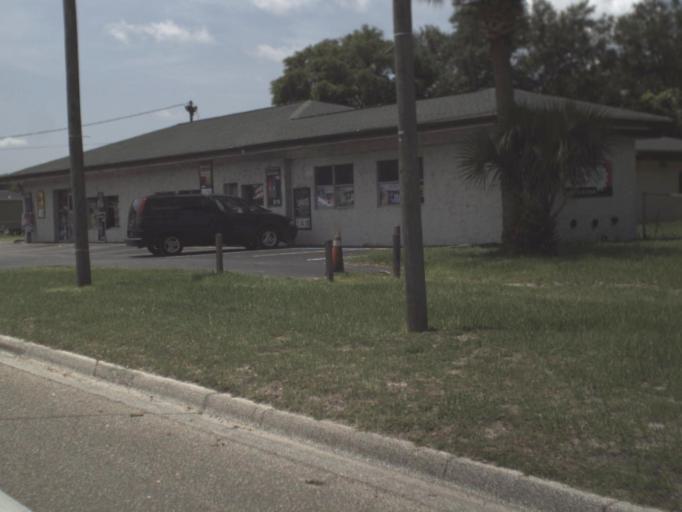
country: US
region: Florida
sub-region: Taylor County
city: Perry
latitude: 30.0749
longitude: -83.5632
